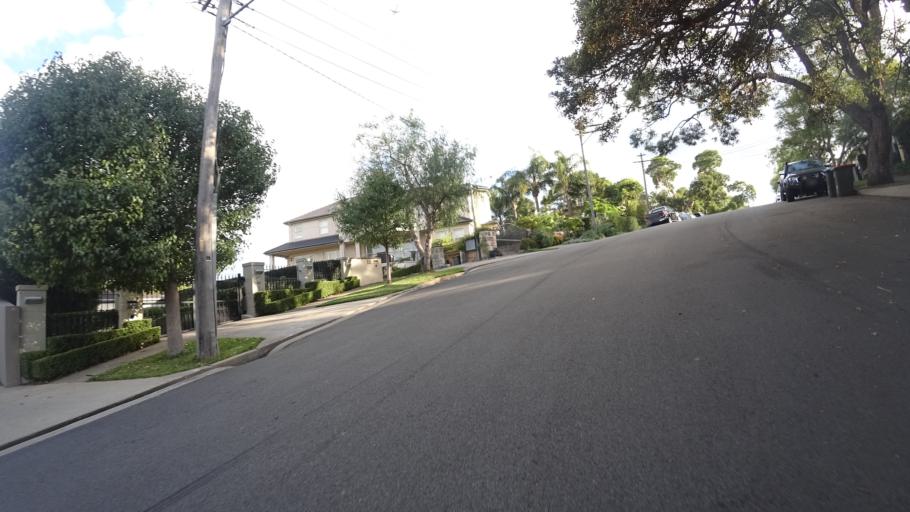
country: AU
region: New South Wales
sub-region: Lane Cove
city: Longueville
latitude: -33.8343
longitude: 151.1609
